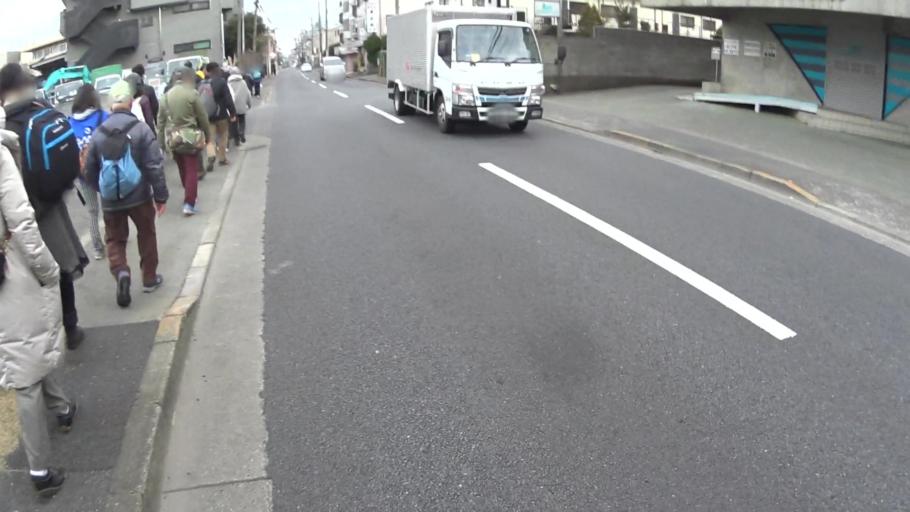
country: JP
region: Tokyo
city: Mitaka-shi
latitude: 35.6727
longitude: 139.5860
